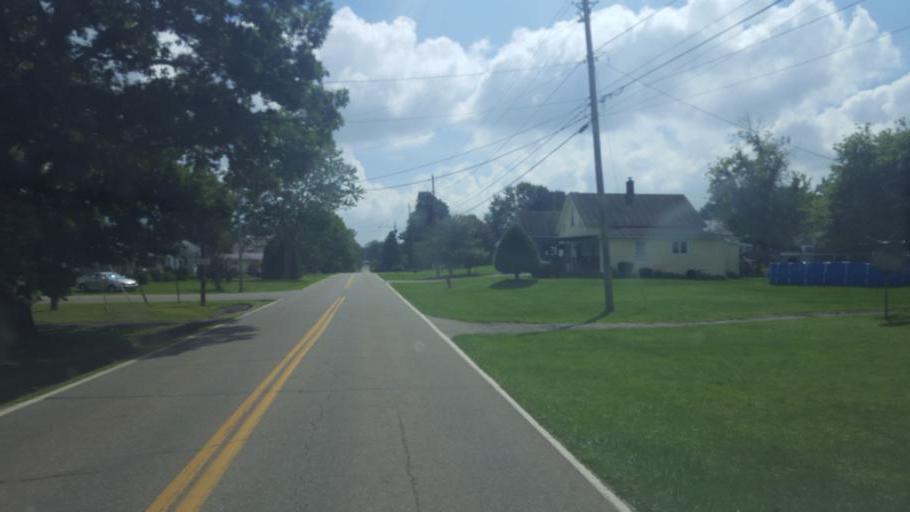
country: US
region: Ohio
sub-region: Knox County
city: Mount Vernon
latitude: 40.4116
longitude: -82.4885
